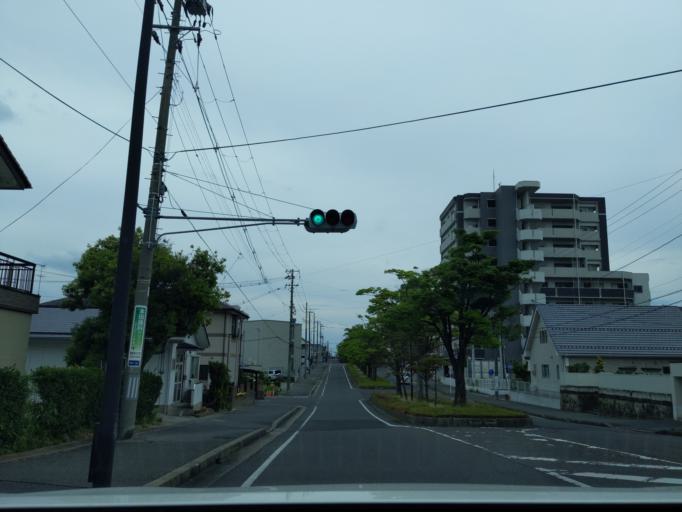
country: JP
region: Fukushima
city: Koriyama
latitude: 37.3905
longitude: 140.3646
